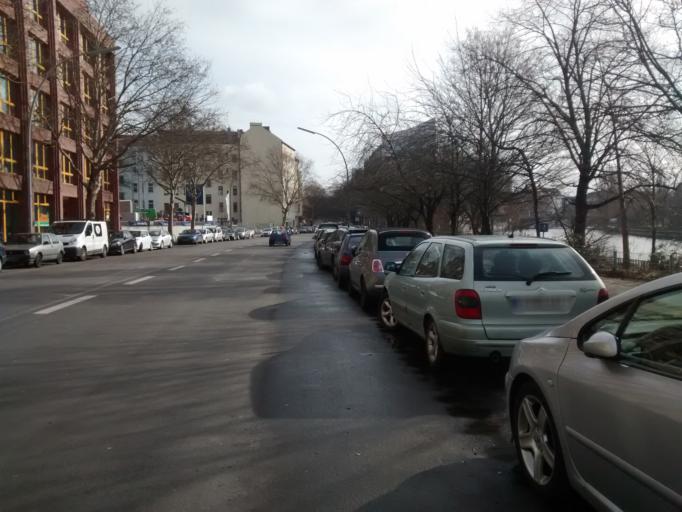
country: DE
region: Berlin
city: Moabit
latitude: 52.5251
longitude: 13.3252
